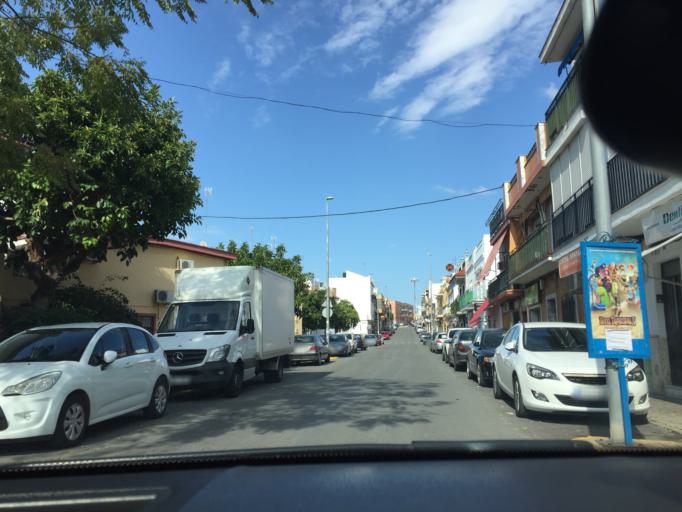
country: ES
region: Andalusia
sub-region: Provincia de Sevilla
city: Coria del Rio
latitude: 37.2922
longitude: -6.0522
